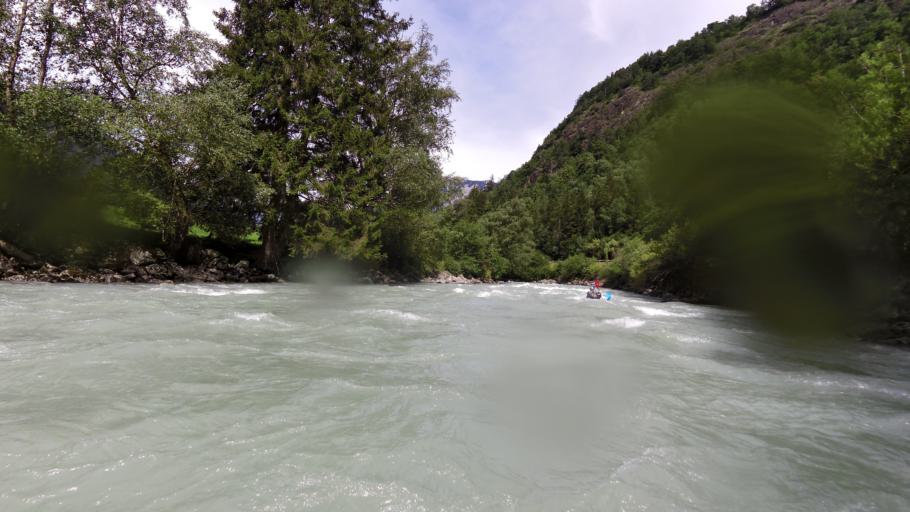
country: AT
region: Tyrol
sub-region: Politischer Bezirk Imst
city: Sautens
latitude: 47.2059
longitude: 10.8793
